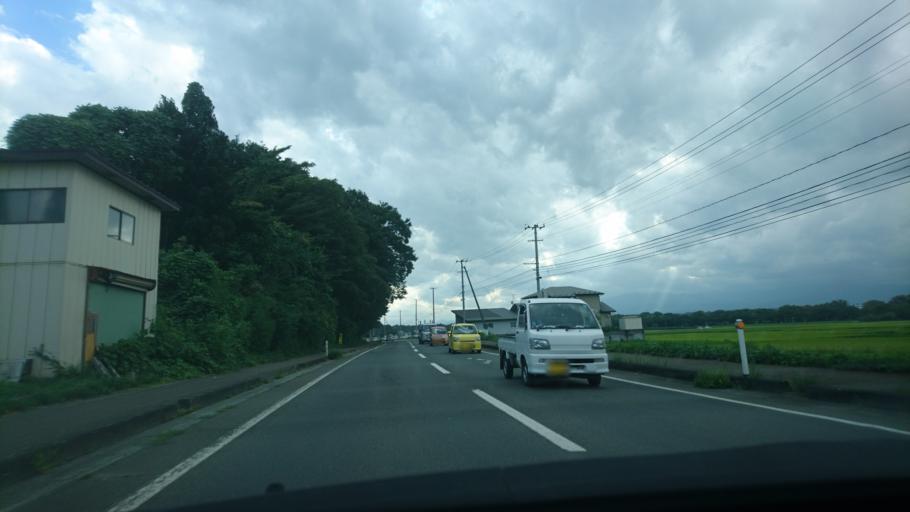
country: JP
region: Iwate
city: Kitakami
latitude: 39.2780
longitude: 141.1334
